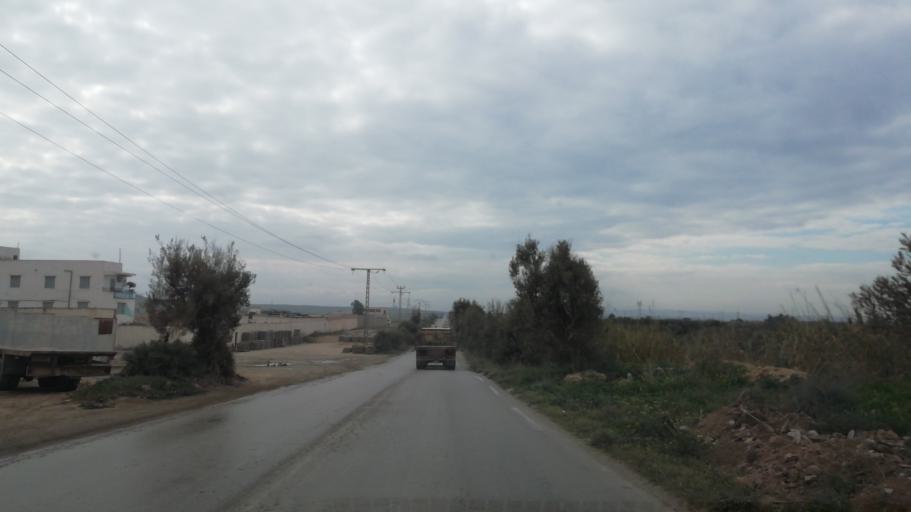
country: DZ
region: Oran
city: Ain el Bya
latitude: 35.7833
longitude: -0.3441
